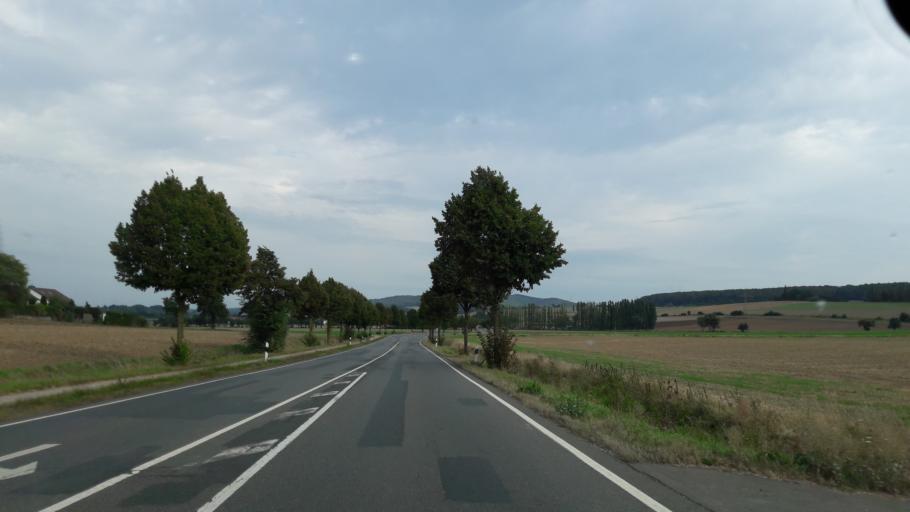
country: DE
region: Lower Saxony
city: Bad Salzdetfurth
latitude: 52.0989
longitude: 9.9932
